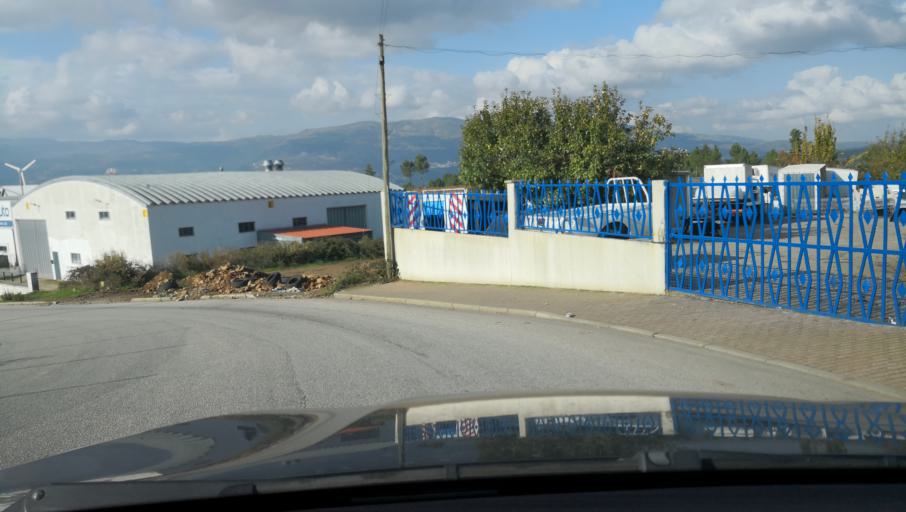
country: PT
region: Vila Real
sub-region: Vila Real
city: Vila Real
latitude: 41.2768
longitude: -7.7109
